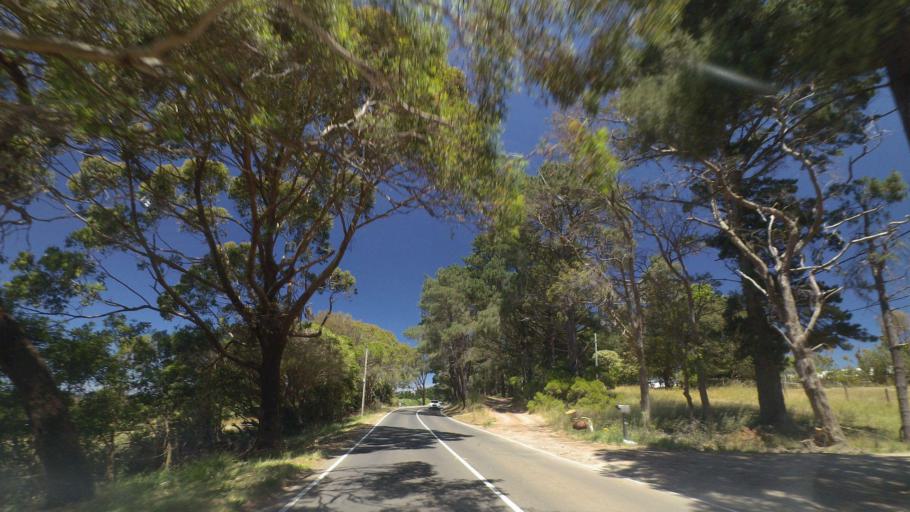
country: AU
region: Victoria
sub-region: Mornington Peninsula
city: Dromana
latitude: -38.3760
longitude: 144.9766
